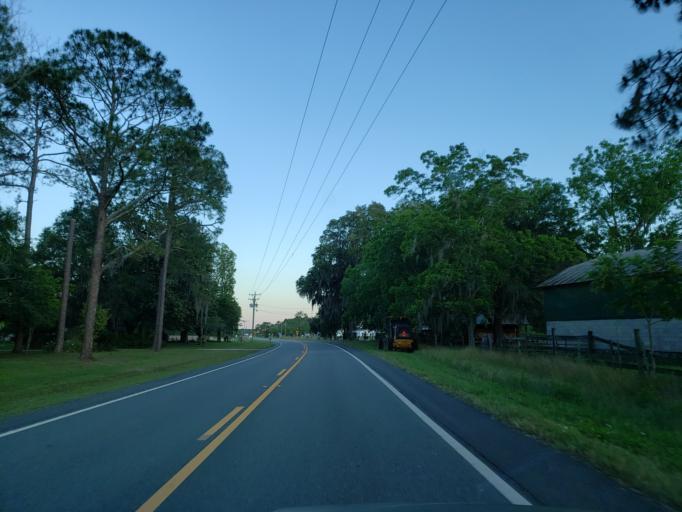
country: US
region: Georgia
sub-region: Echols County
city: Statenville
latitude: 30.5713
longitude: -83.1623
